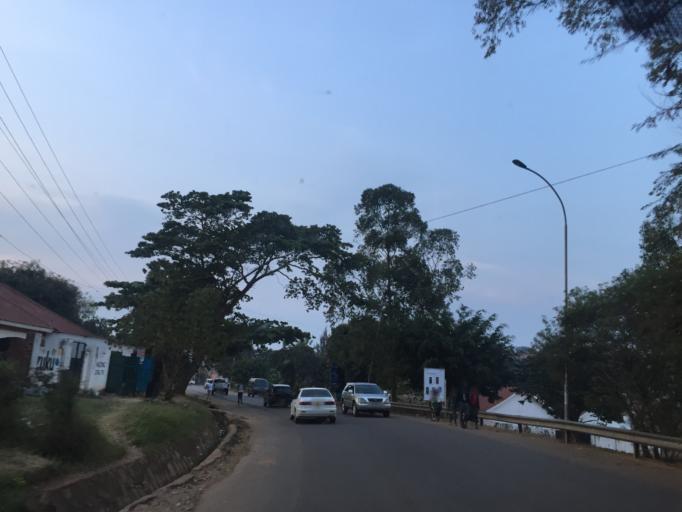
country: UG
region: Central Region
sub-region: Kampala District
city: Kampala
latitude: 0.2535
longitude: 32.6269
